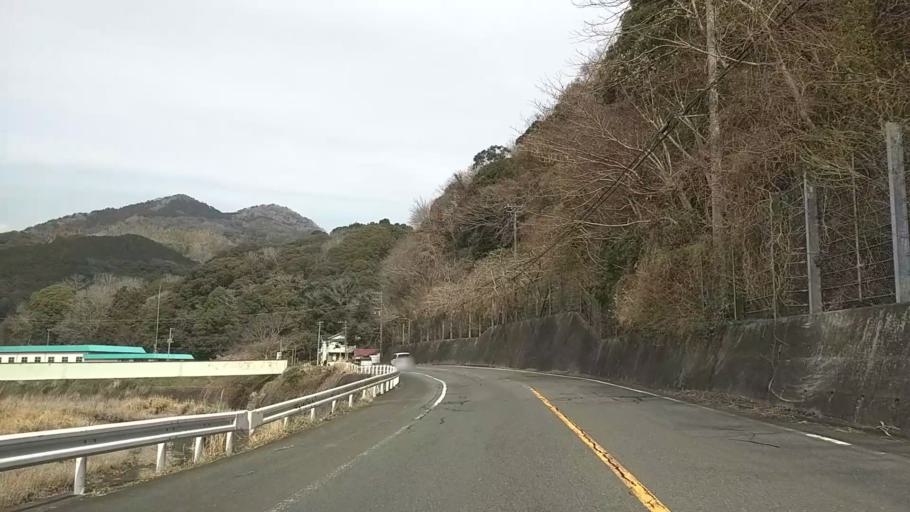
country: JP
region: Shizuoka
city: Shimoda
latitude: 34.7202
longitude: 138.9464
